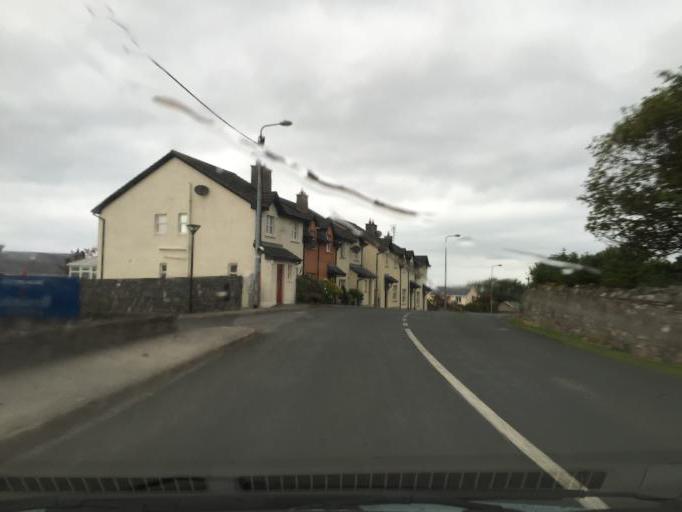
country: IE
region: Connaught
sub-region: Sligo
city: Strandhill
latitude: 54.2636
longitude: -8.5973
